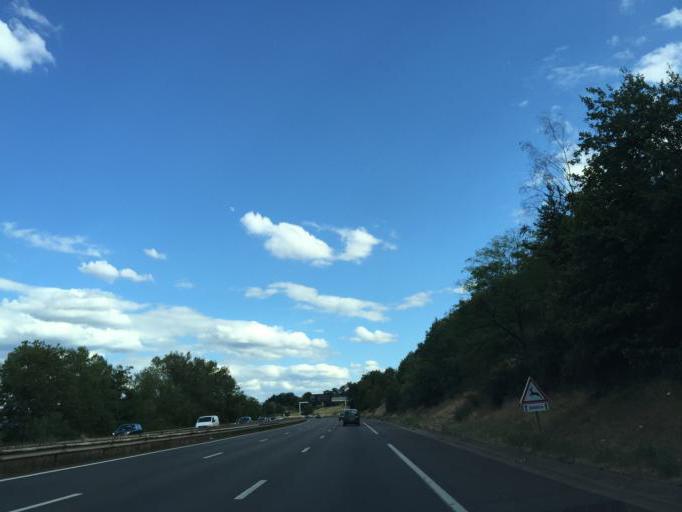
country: FR
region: Rhone-Alpes
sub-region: Departement de la Loire
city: La Fouillouse
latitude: 45.4920
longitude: 4.3192
